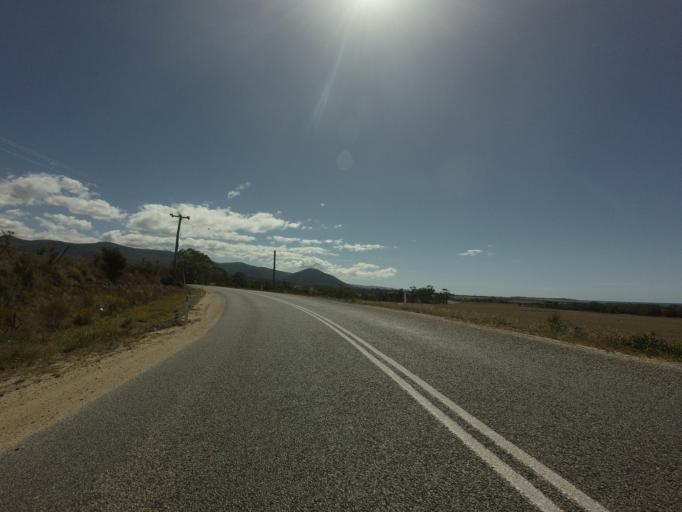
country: AU
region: Tasmania
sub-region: Break O'Day
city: St Helens
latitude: -41.7870
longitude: 148.2620
